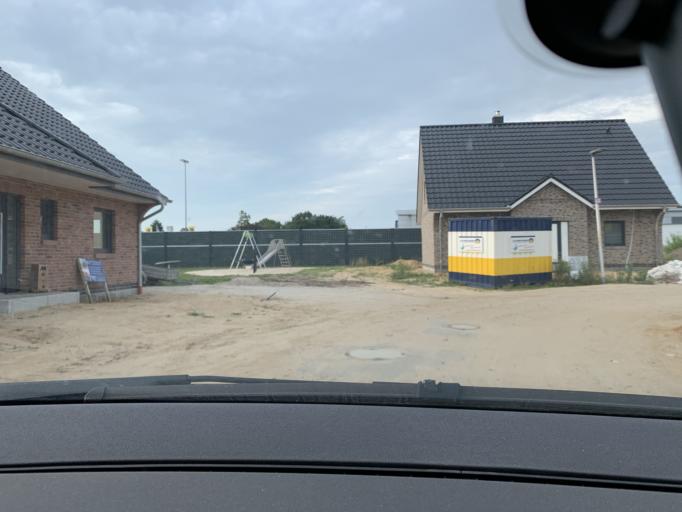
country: DE
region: Schleswig-Holstein
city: Mildstedt
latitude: 54.4694
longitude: 9.0908
